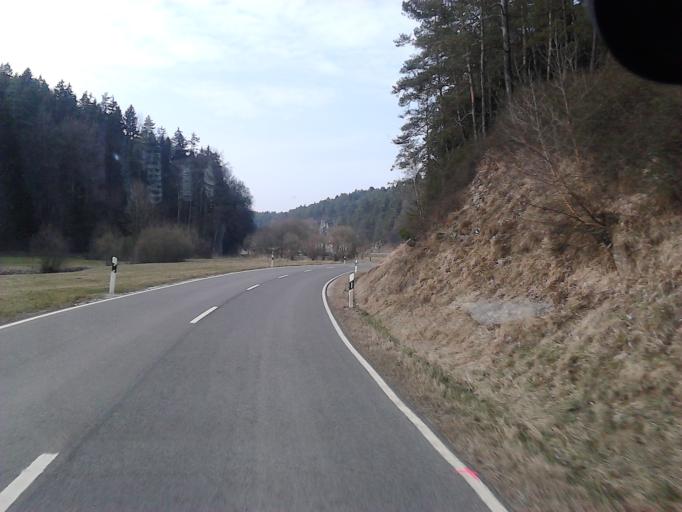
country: DE
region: Bavaria
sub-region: Upper Franconia
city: Konigsfeld
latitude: 49.9607
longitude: 11.2054
